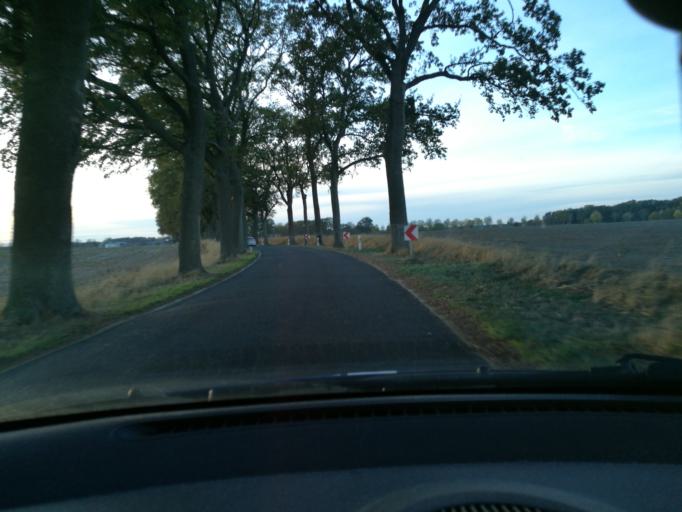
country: DE
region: Brandenburg
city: Karstadt
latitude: 53.0972
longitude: 11.7108
